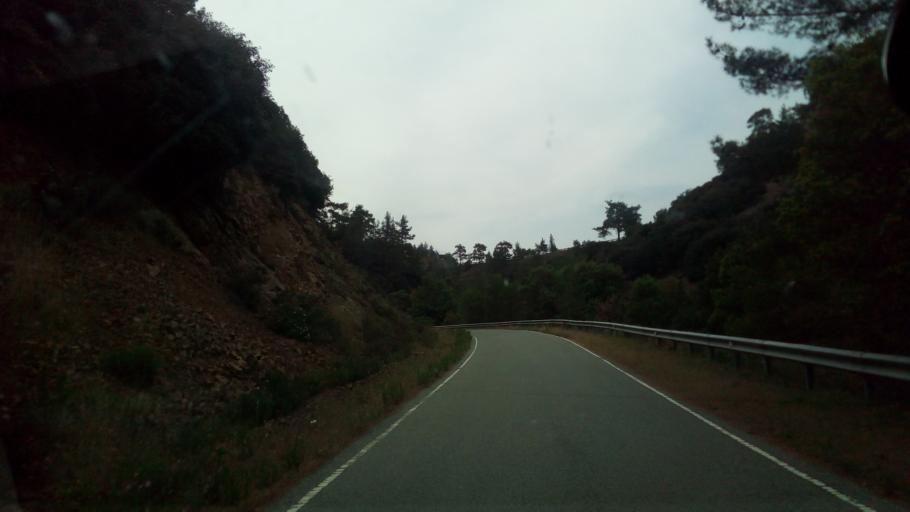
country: CY
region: Lefkosia
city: Kakopetria
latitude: 34.9833
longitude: 32.7510
